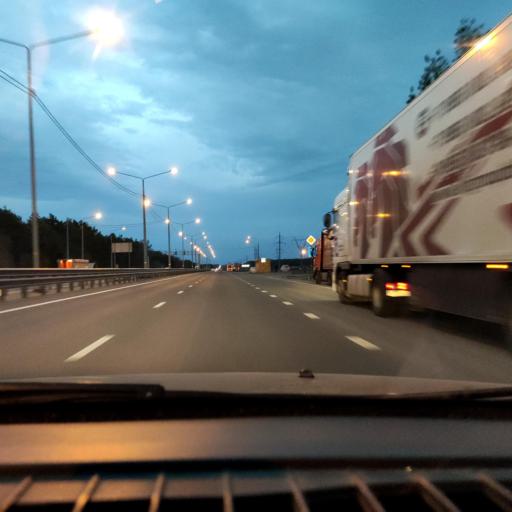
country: RU
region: Samara
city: Zhigulevsk
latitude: 53.5137
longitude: 49.6111
